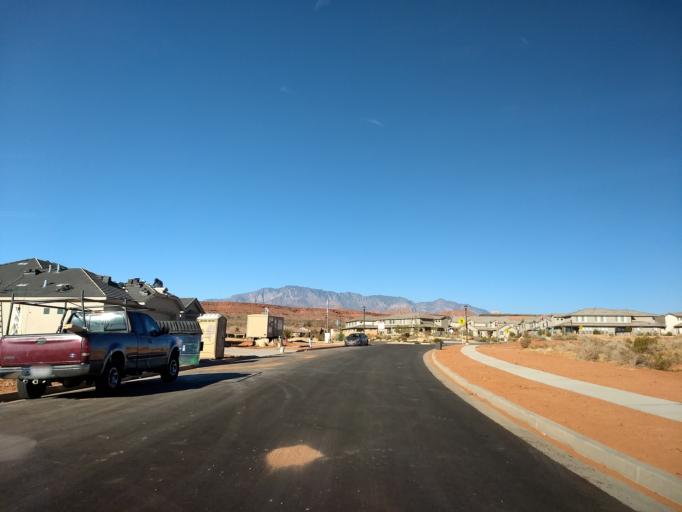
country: US
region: Utah
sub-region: Washington County
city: Washington
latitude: 37.1430
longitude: -113.4793
